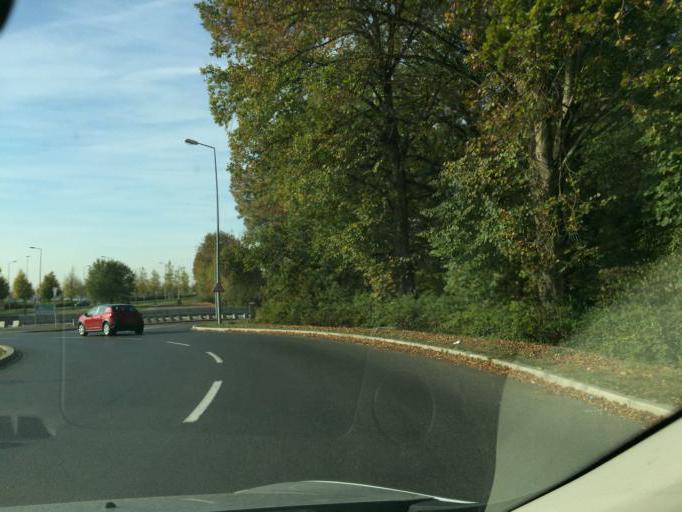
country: LU
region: Luxembourg
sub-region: Canton de Luxembourg
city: Sandweiler
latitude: 49.6372
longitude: 6.2161
